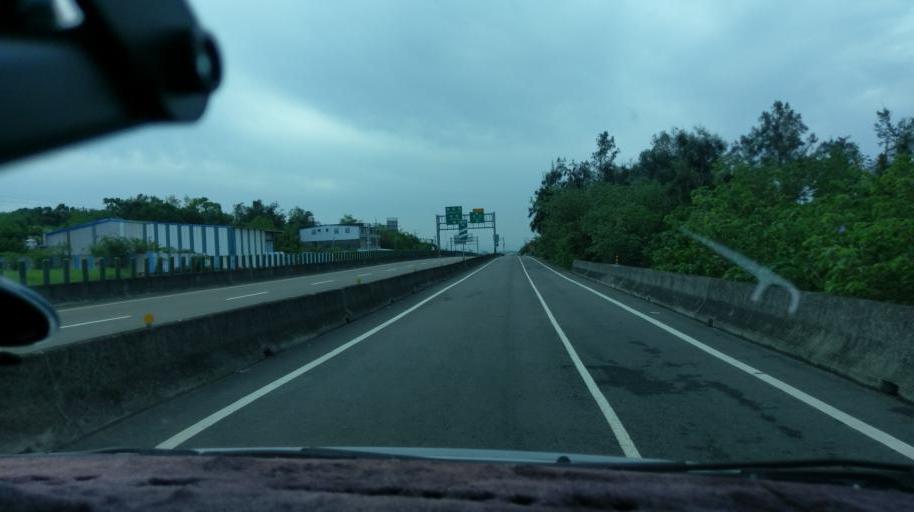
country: TW
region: Taiwan
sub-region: Hsinchu
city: Hsinchu
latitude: 24.7189
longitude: 120.8679
